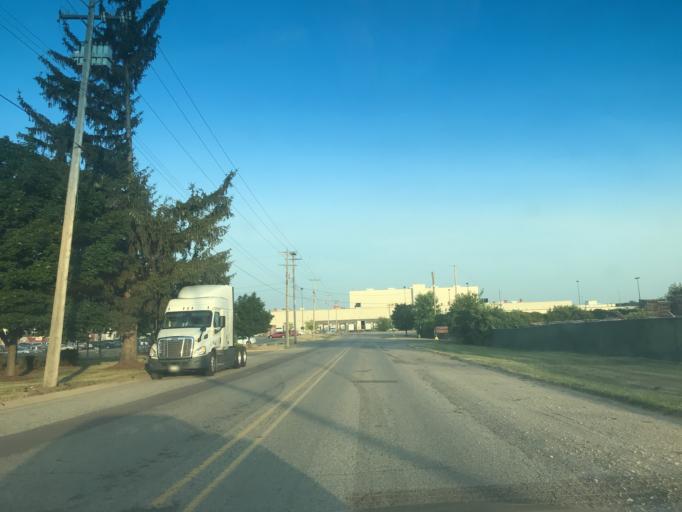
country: US
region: Michigan
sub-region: Eaton County
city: Waverly
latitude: 42.6976
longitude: -84.6317
